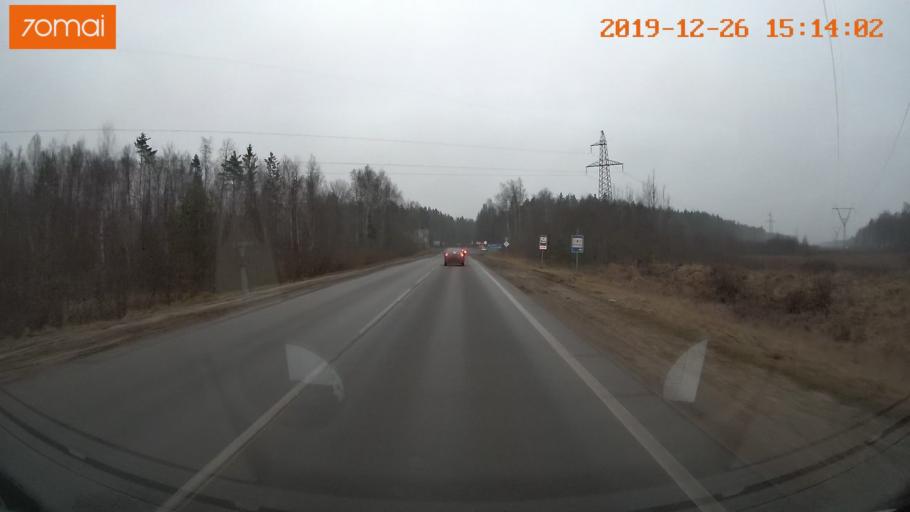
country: RU
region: Jaroslavl
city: Rybinsk
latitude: 58.1097
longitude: 38.8820
